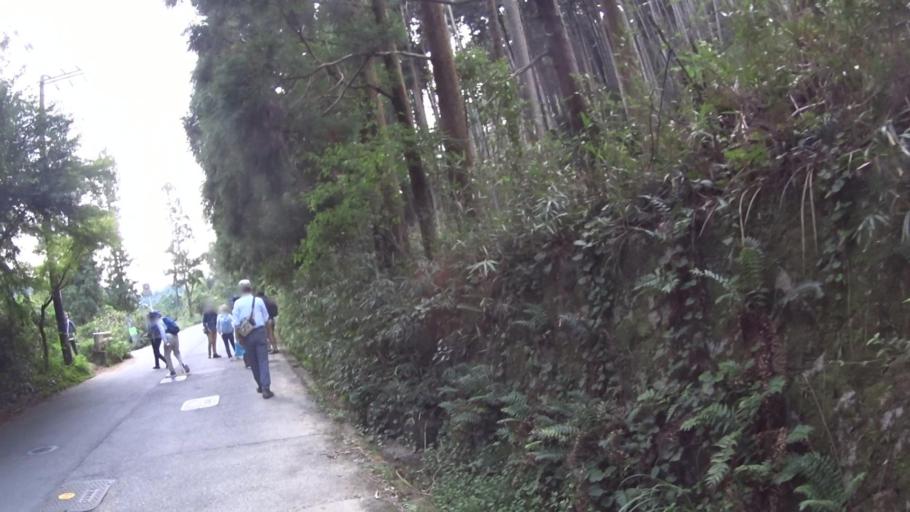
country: JP
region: Osaka
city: Kaizuka
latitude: 34.4776
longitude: 135.3101
